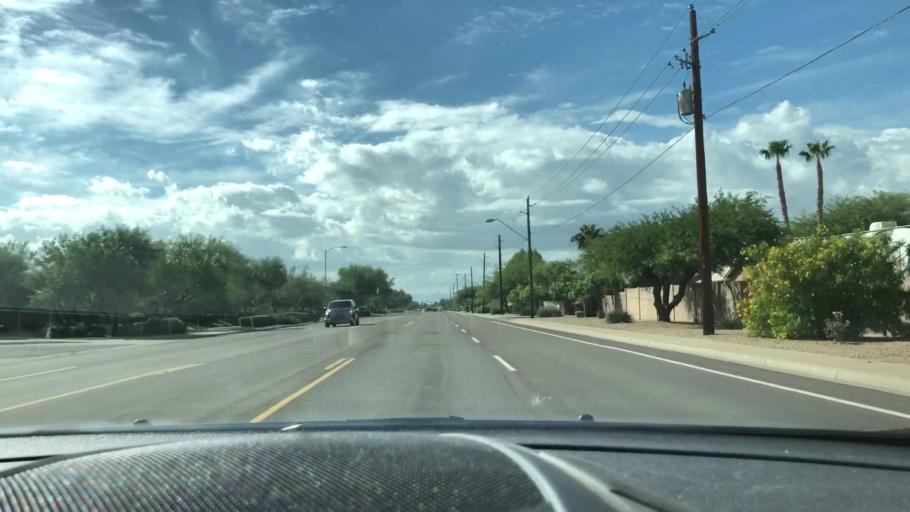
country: US
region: Arizona
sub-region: Maricopa County
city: Sun City
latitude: 33.6874
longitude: -112.2377
